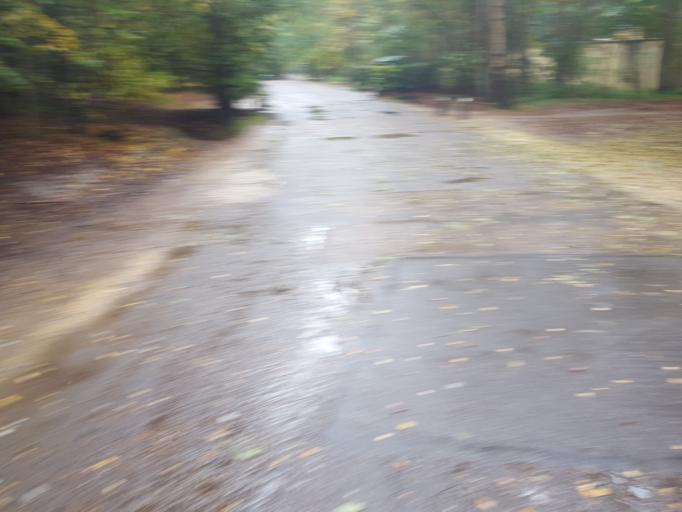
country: GB
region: England
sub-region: Norfolk
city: Weeting
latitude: 52.3911
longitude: 0.6357
